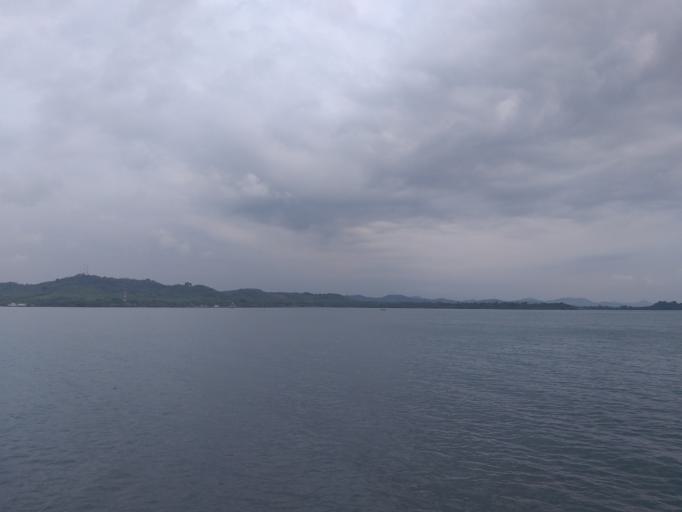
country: TH
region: Trat
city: Laem Ngop
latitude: 12.1677
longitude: 102.2954
